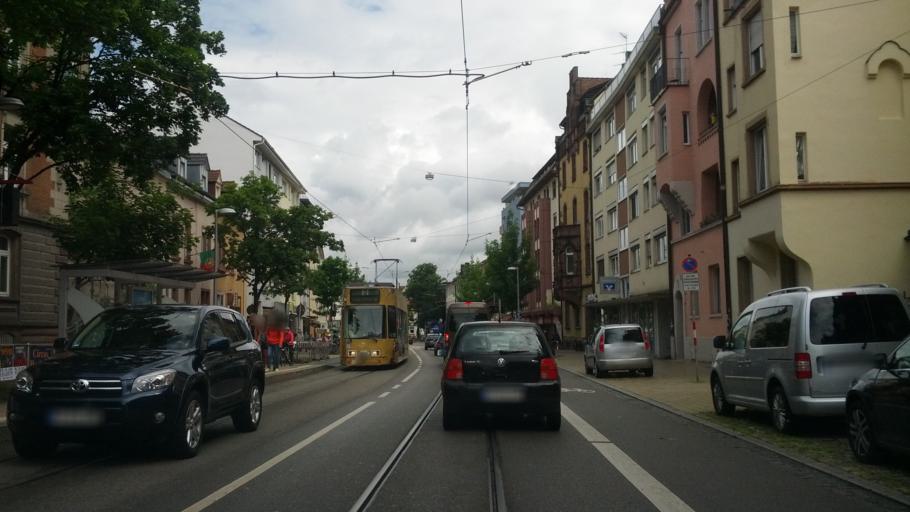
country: DE
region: Baden-Wuerttemberg
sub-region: Freiburg Region
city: Freiburg
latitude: 48.0063
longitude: 7.8553
